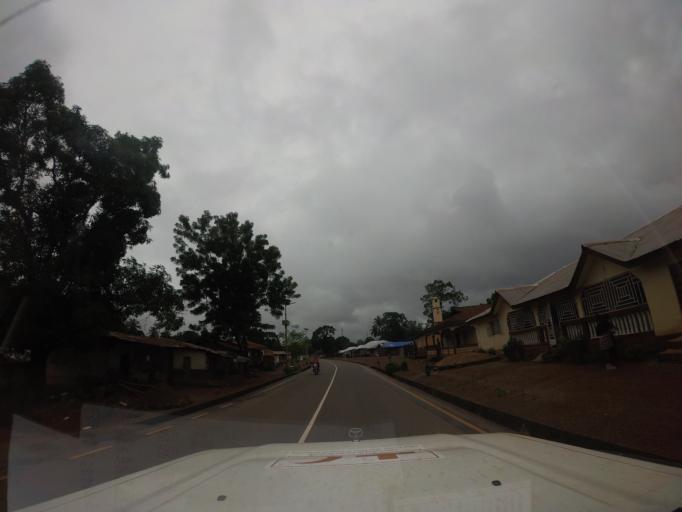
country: SL
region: Northern Province
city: Kambia
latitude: 9.1236
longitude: -12.9163
